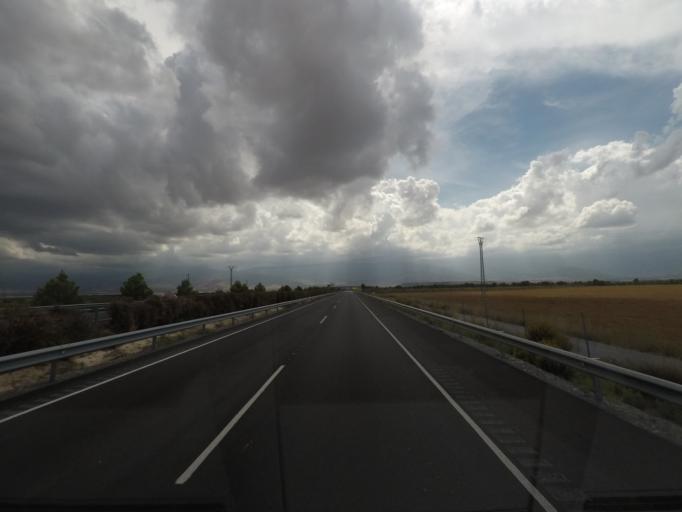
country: ES
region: Andalusia
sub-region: Provincia de Granada
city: Albunan
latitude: 37.2517
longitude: -3.0817
